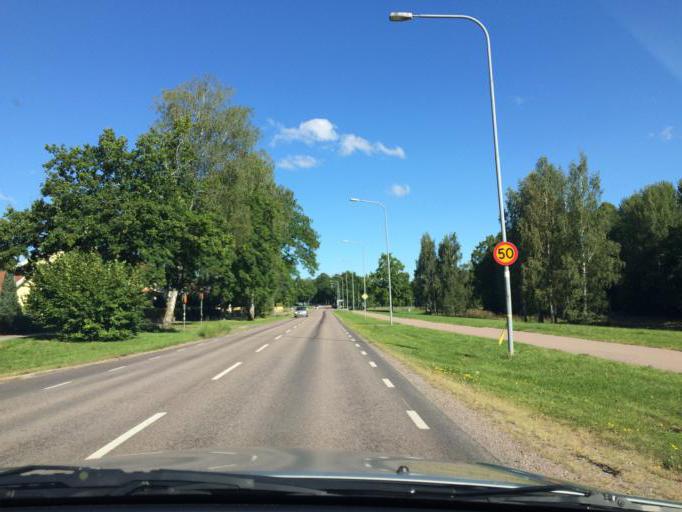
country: SE
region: Vaestmanland
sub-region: Vasteras
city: Vasteras
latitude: 59.5964
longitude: 16.5960
